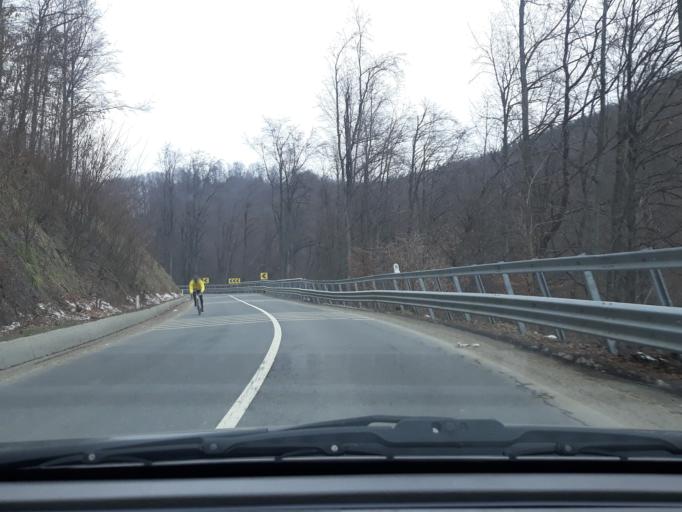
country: RO
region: Bihor
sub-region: Oras Alesd
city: Padurea Neagra
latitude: 47.1247
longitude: 22.4171
